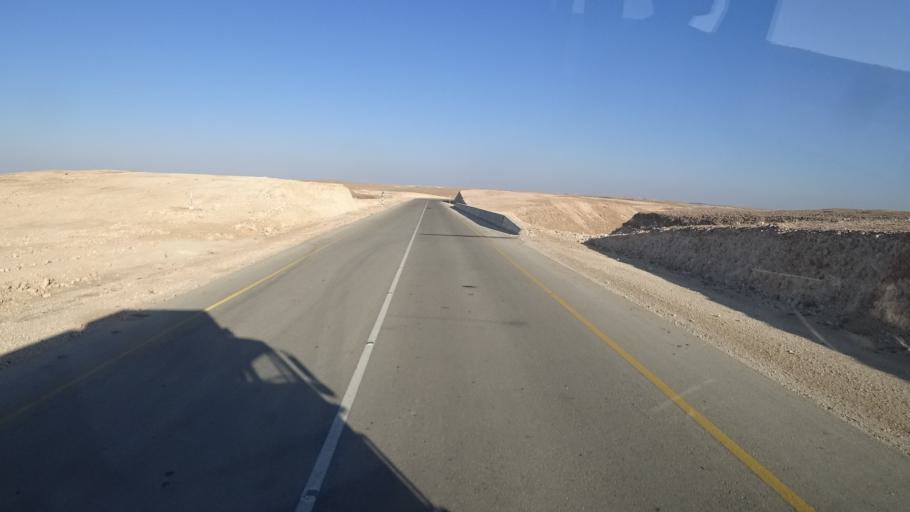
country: YE
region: Al Mahrah
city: Hawf
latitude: 17.0810
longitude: 53.0141
